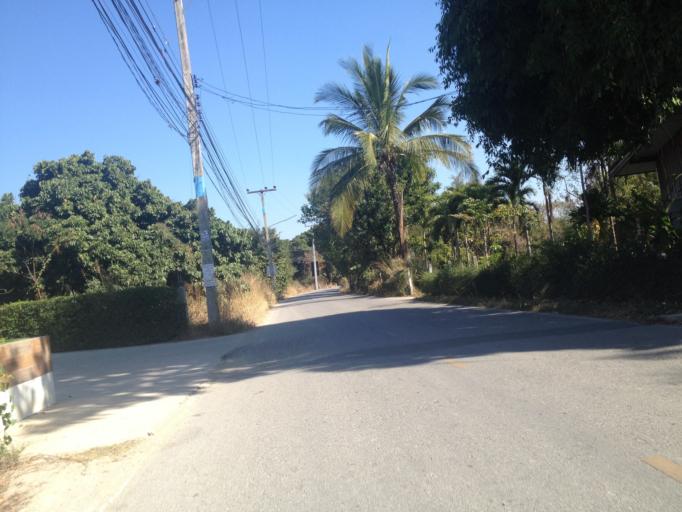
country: TH
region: Chiang Mai
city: Hang Dong
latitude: 18.6867
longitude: 98.8887
